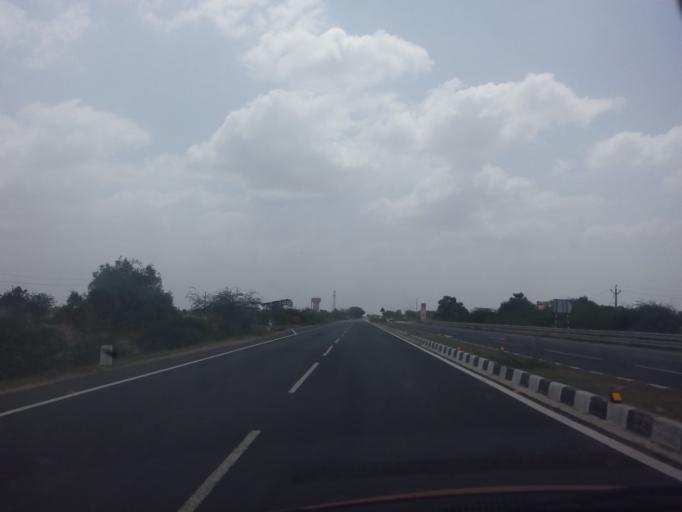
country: IN
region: Gujarat
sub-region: Ahmadabad
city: Mandal
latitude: 23.0847
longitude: 71.8703
